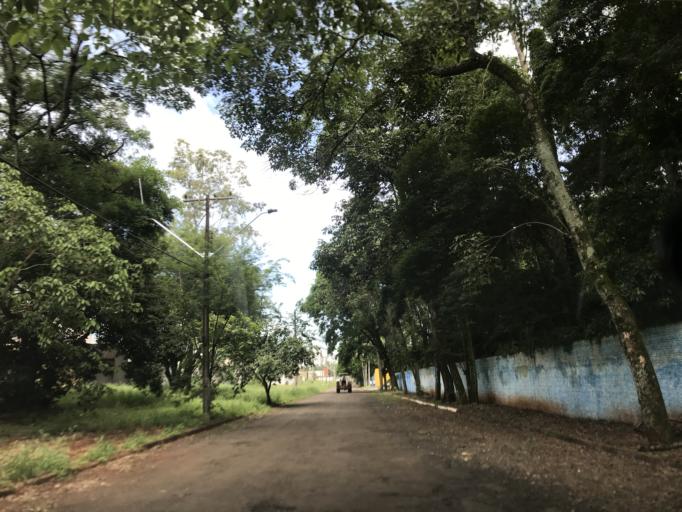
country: BR
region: Parana
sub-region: Londrina
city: Londrina
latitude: -23.3439
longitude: -51.1547
